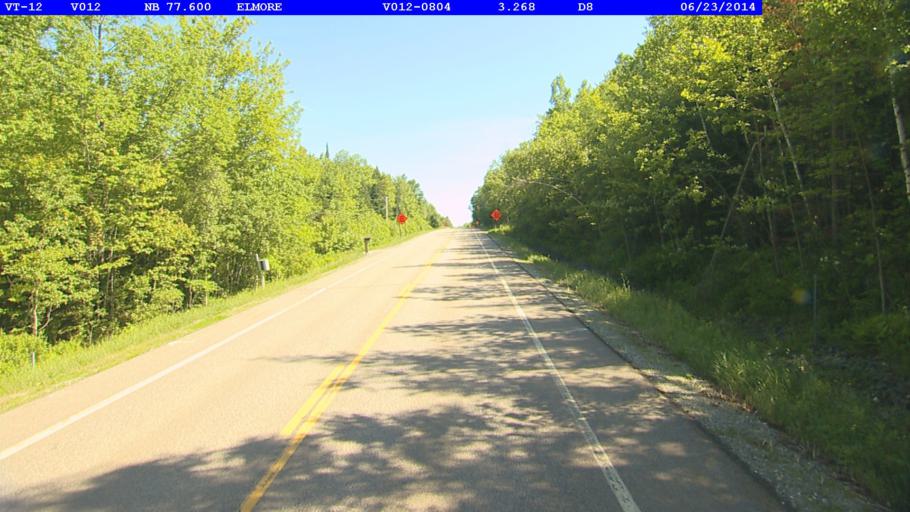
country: US
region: Vermont
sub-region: Lamoille County
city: Morrisville
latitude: 44.4929
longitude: -72.5207
